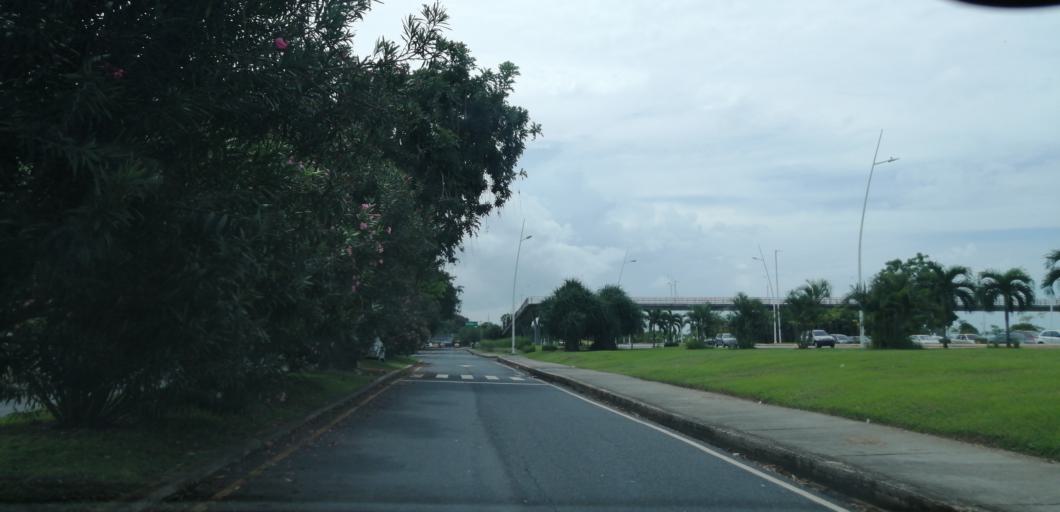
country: PA
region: Panama
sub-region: Distrito de Panama
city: Ancon
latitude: 8.9487
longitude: -79.5439
